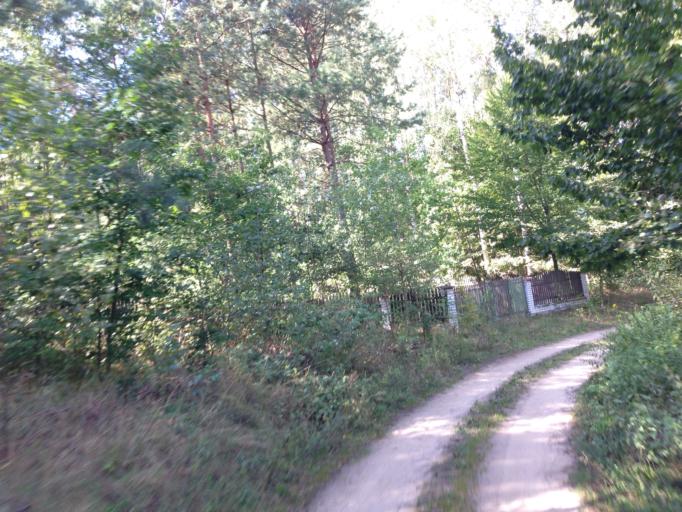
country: PL
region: Warmian-Masurian Voivodeship
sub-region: Powiat dzialdowski
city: Lidzbark
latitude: 53.2263
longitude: 19.7472
